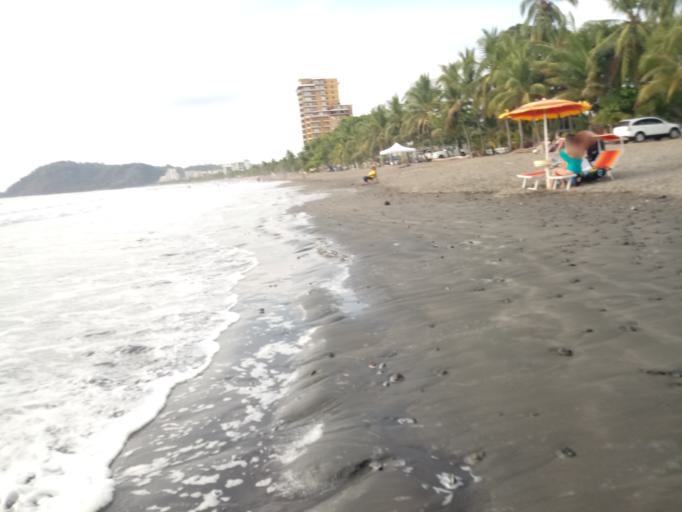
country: CR
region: Puntarenas
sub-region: Canton de Garabito
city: Jaco
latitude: 9.6074
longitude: -84.6250
